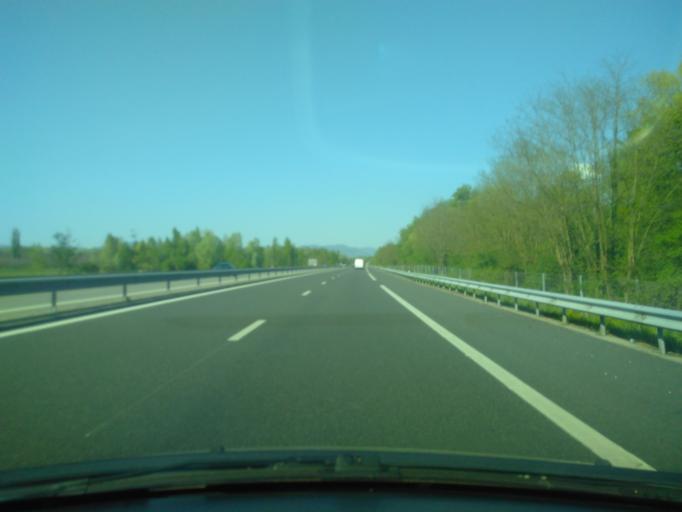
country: FR
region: Rhone-Alpes
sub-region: Departement de l'Isere
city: Saint-Quentin-sur-Isere
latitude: 45.2519
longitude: 5.5059
